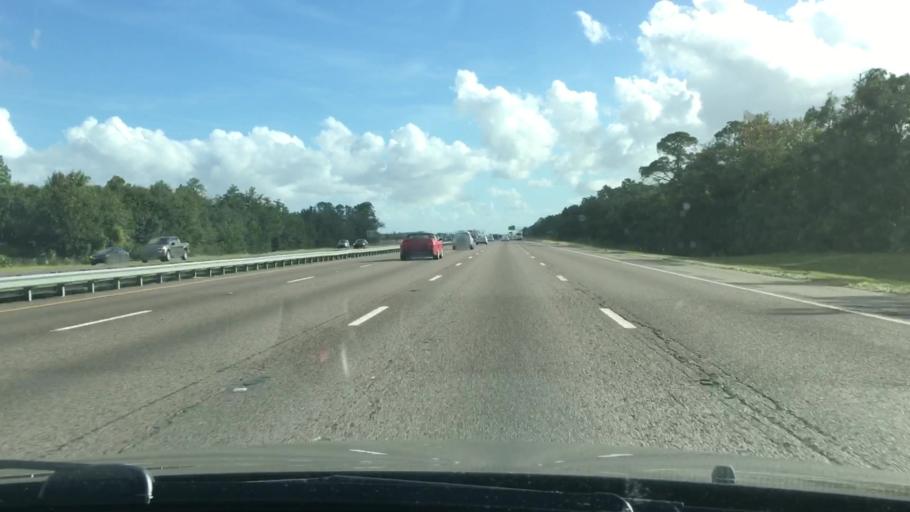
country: US
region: Florida
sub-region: Volusia County
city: Ormond Beach
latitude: 29.2401
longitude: -81.1103
